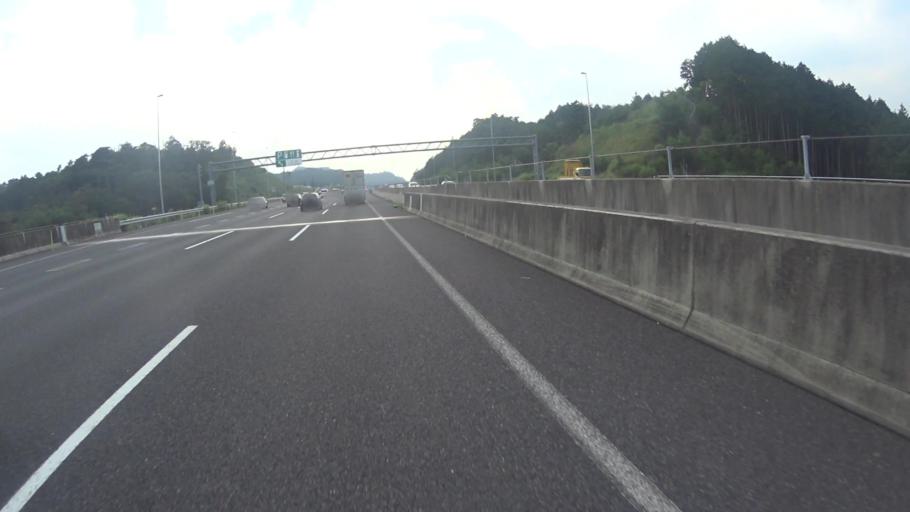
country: JP
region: Shiga Prefecture
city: Hino
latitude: 34.9153
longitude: 136.2997
